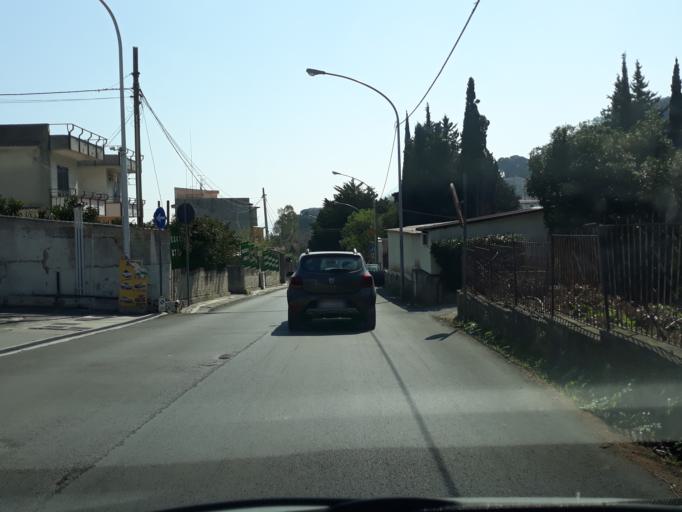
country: IT
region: Sicily
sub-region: Palermo
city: Piano dei Geli
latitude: 38.1179
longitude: 13.2889
